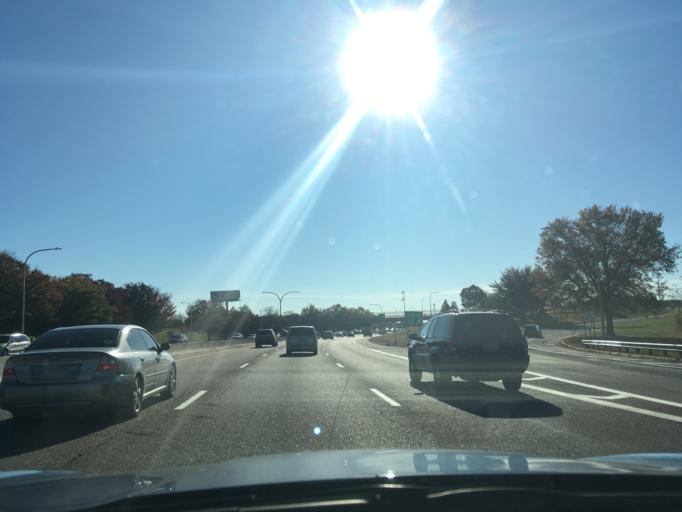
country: US
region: Rhode Island
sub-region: Providence County
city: Pawtucket
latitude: 41.8578
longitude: -71.4048
